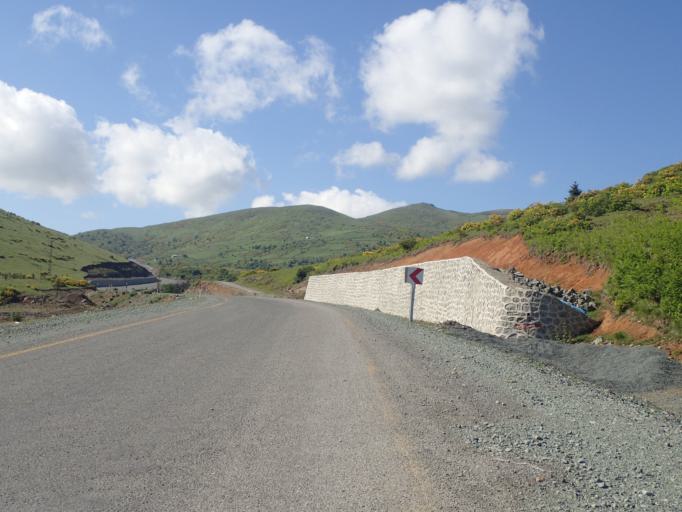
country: TR
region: Ordu
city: Topcam
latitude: 40.6787
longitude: 37.9287
